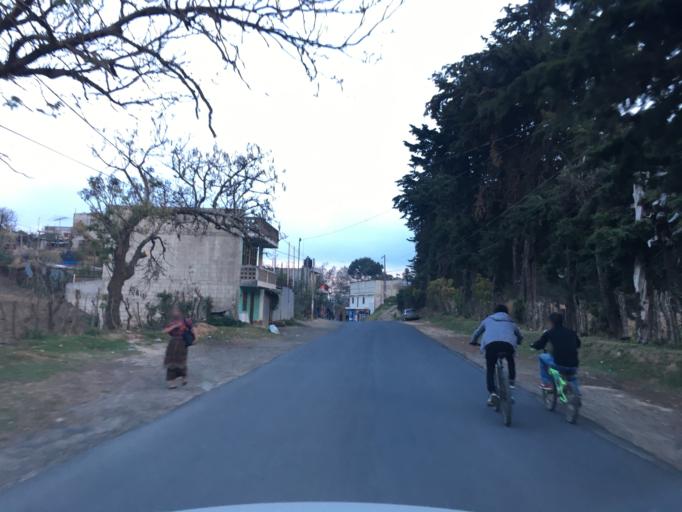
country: GT
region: Chimaltenango
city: Tecpan Guatemala
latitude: 14.7509
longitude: -91.0008
